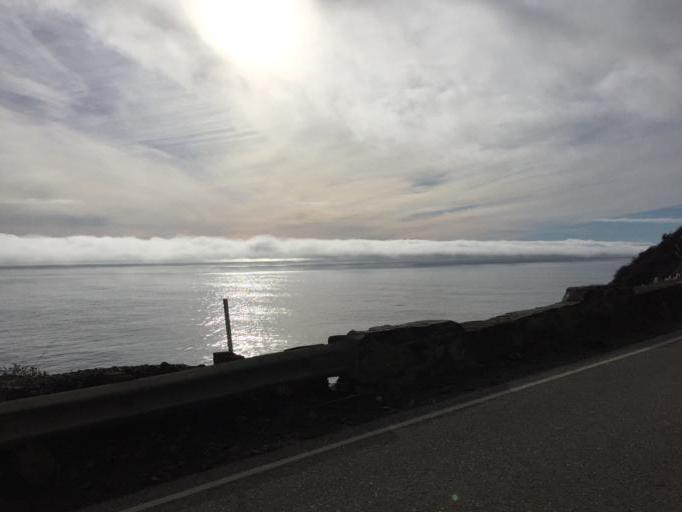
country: US
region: California
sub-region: Monterey County
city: King City
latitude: 35.8663
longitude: -121.4345
